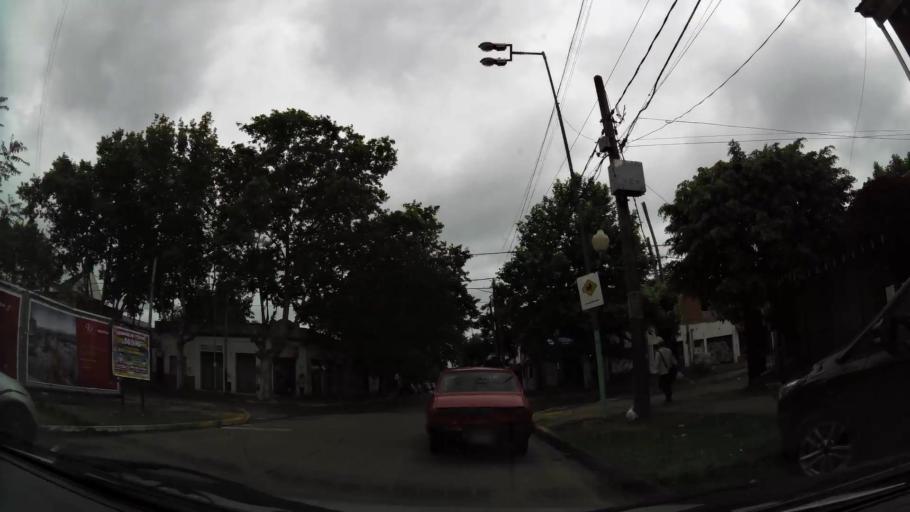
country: AR
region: Buenos Aires
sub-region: Partido de Lomas de Zamora
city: Lomas de Zamora
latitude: -34.7620
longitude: -58.3911
